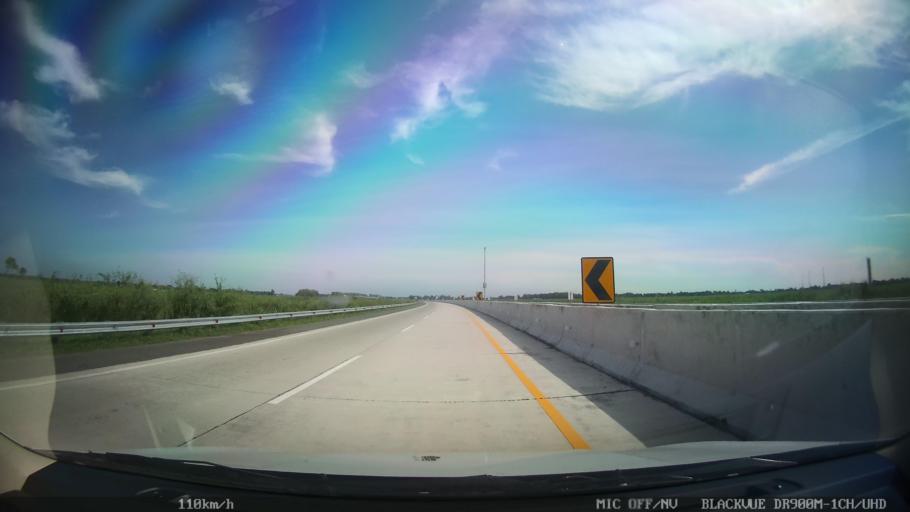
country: ID
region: North Sumatra
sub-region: Kabupaten Langkat
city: Stabat
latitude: 3.6943
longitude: 98.5413
